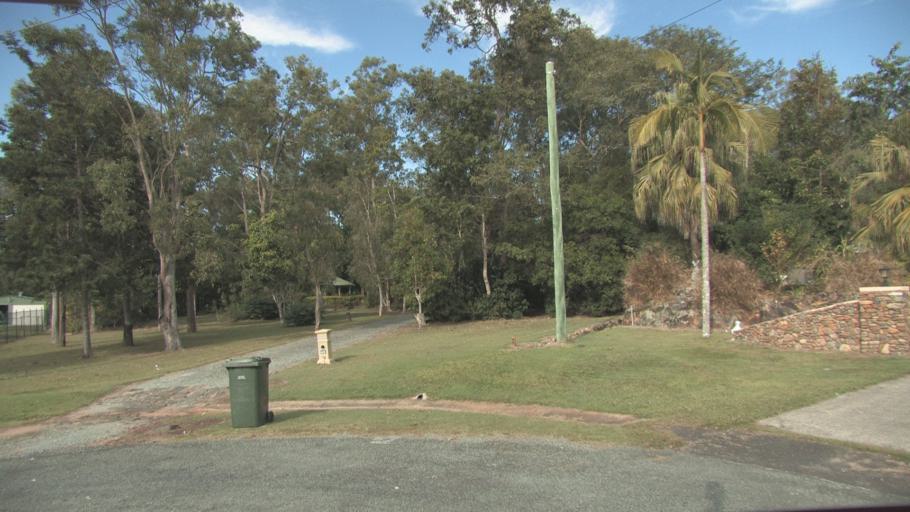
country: AU
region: Queensland
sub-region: Logan
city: Park Ridge South
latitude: -27.7378
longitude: 153.0352
